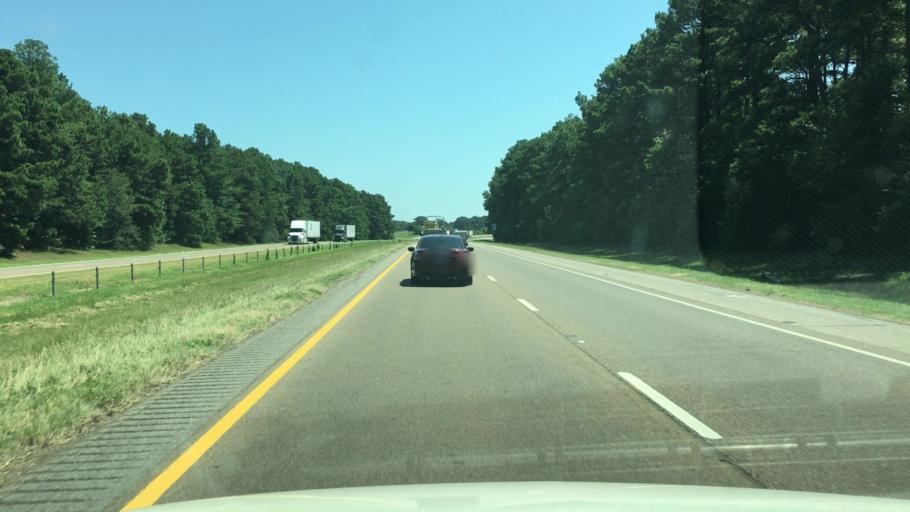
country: US
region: Texas
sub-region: Bowie County
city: New Boston
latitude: 33.4736
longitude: -94.4504
